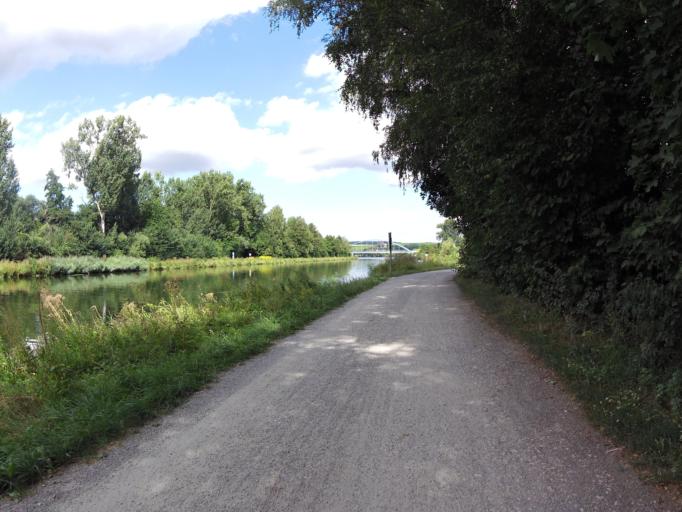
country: DE
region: Bavaria
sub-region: Regierungsbezirk Unterfranken
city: Volkach
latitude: 49.8580
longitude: 10.2238
